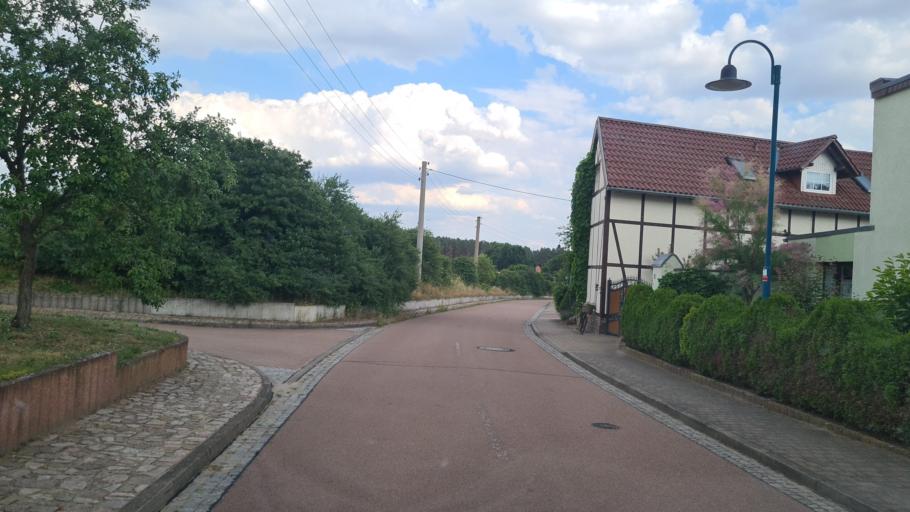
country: DE
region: Saxony-Anhalt
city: Kropstadt
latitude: 51.9527
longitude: 12.6976
